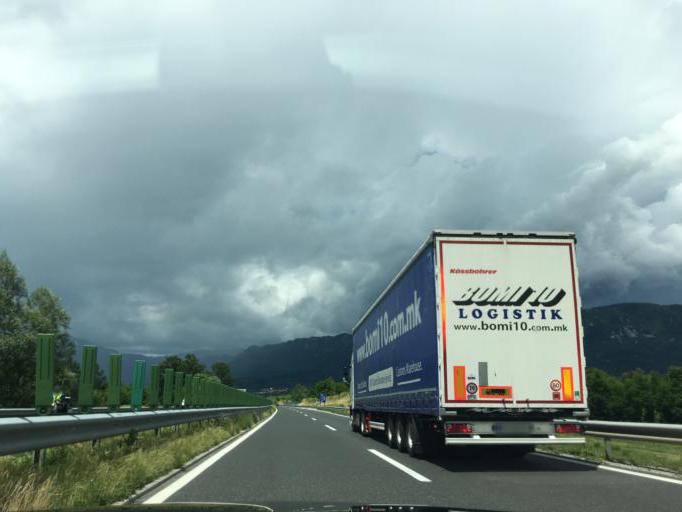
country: SI
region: Vipava
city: Vipava
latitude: 45.8420
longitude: 13.9520
